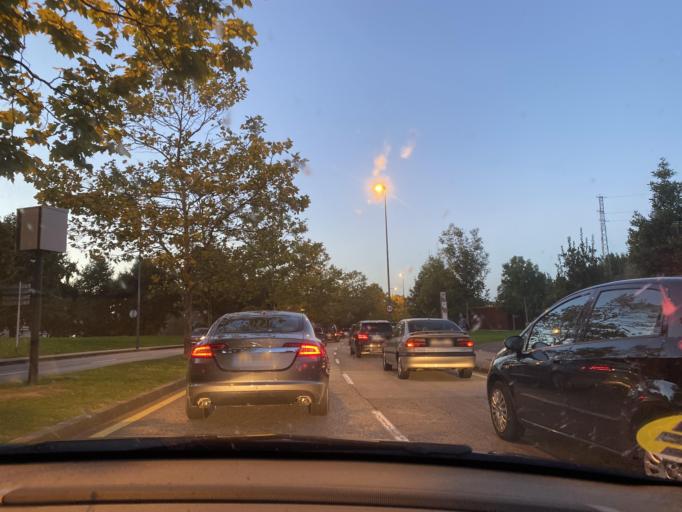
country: ES
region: Asturias
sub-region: Province of Asturias
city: Gijon
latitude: 43.5223
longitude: -5.6633
